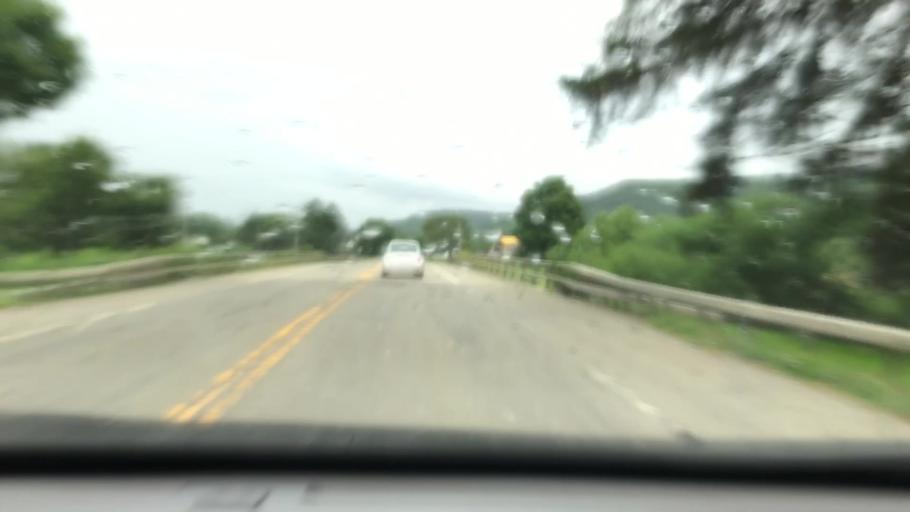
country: US
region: New York
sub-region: Cattaraugus County
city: Salamanca
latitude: 42.1936
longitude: -78.6648
